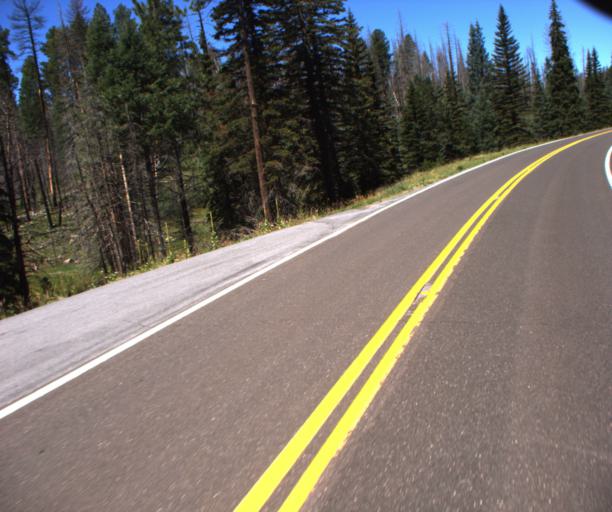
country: US
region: Arizona
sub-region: Apache County
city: Eagar
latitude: 33.6464
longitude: -109.2951
